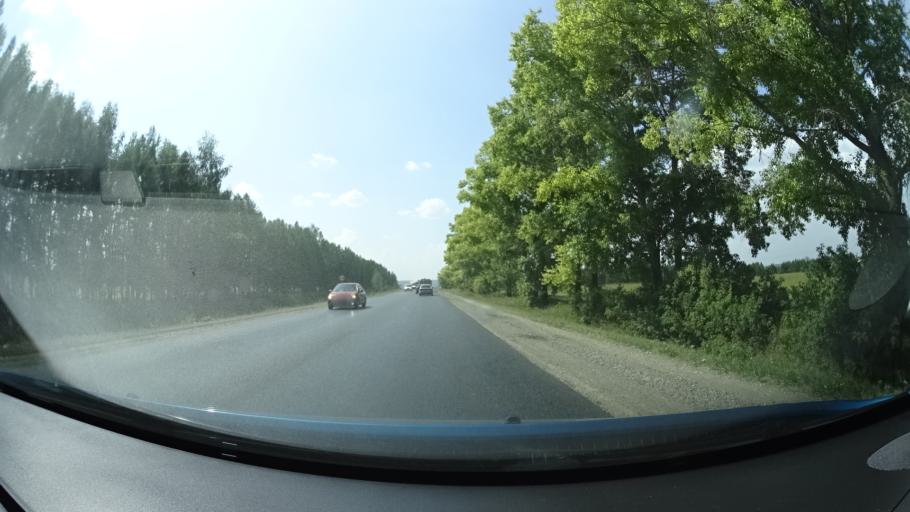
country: RU
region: Bashkortostan
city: Kandry
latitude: 54.5243
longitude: 54.0609
